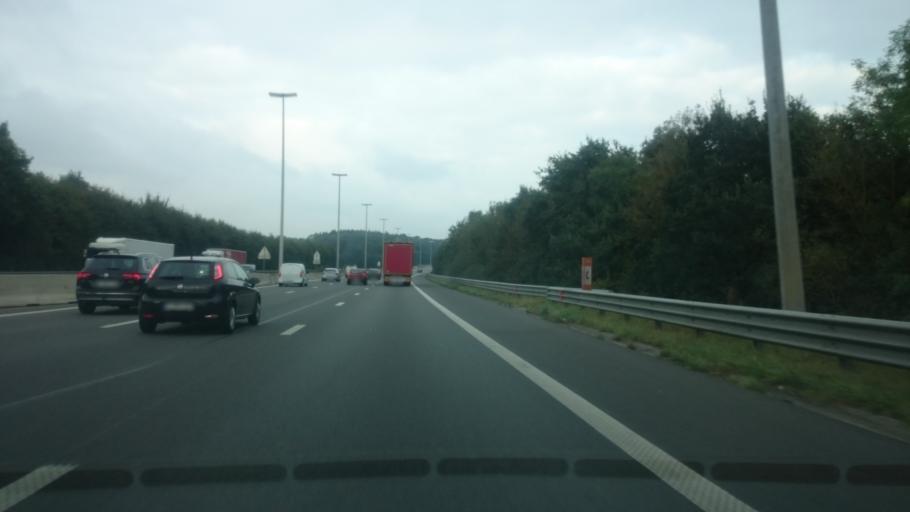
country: BE
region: Wallonia
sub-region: Province de Namur
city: Namur
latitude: 50.5006
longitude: 4.8127
